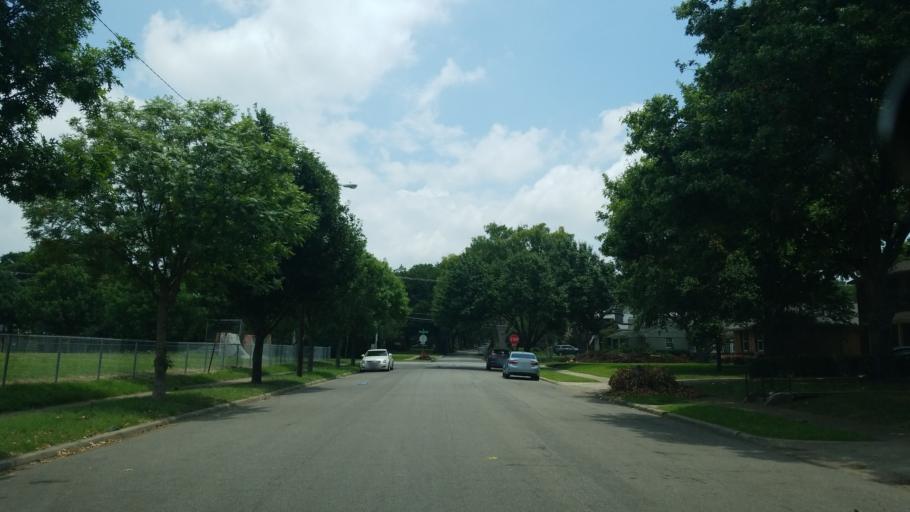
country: US
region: Texas
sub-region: Dallas County
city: University Park
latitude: 32.8474
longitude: -96.8199
